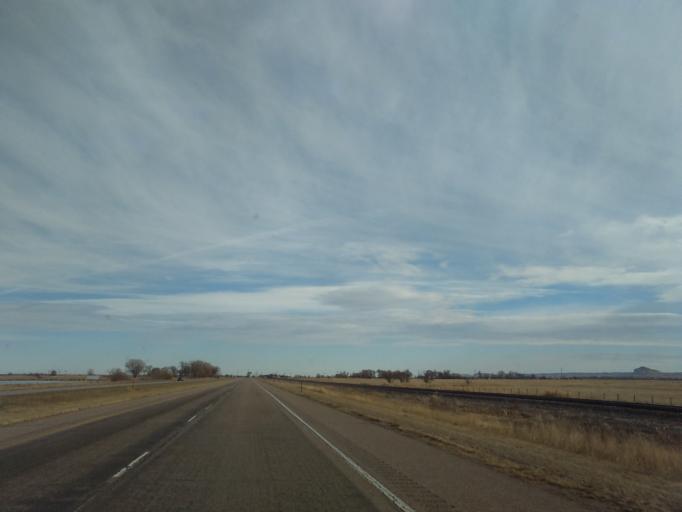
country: US
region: Nebraska
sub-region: Scotts Bluff County
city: Gering
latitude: 41.8228
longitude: -103.5513
